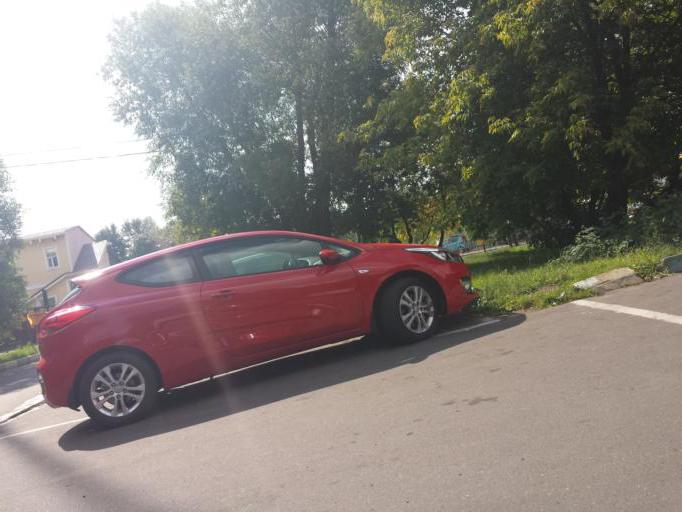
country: RU
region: Moskovskaya
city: Novogireyevo
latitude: 55.7464
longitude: 37.8233
